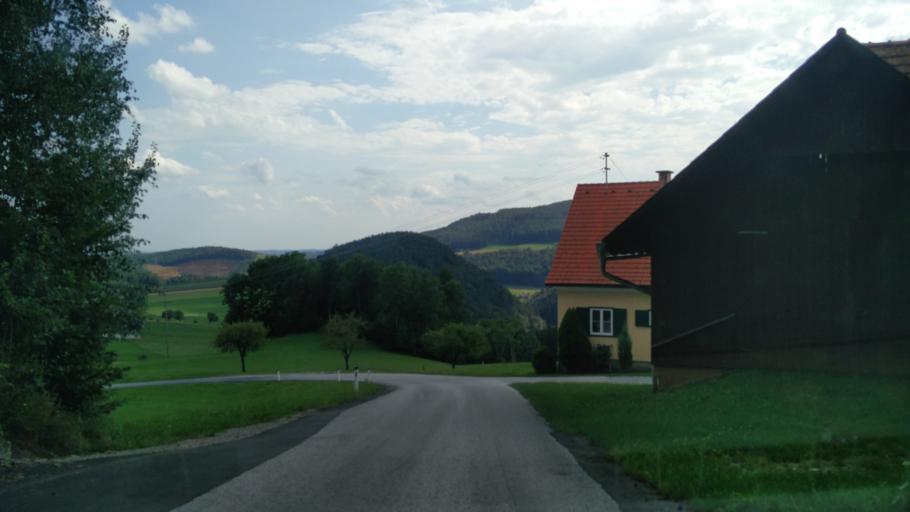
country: AT
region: Styria
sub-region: Politischer Bezirk Weiz
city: Naas
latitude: 47.2520
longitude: 15.6020
